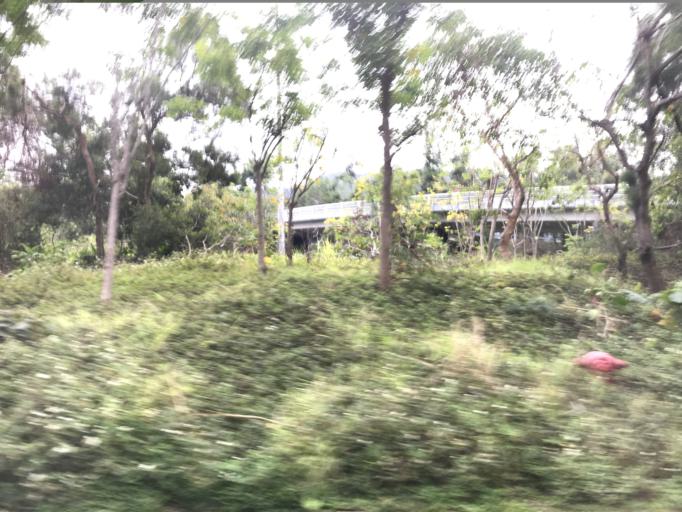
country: HK
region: Tai Po
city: Tai Po
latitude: 22.4460
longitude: 114.1763
